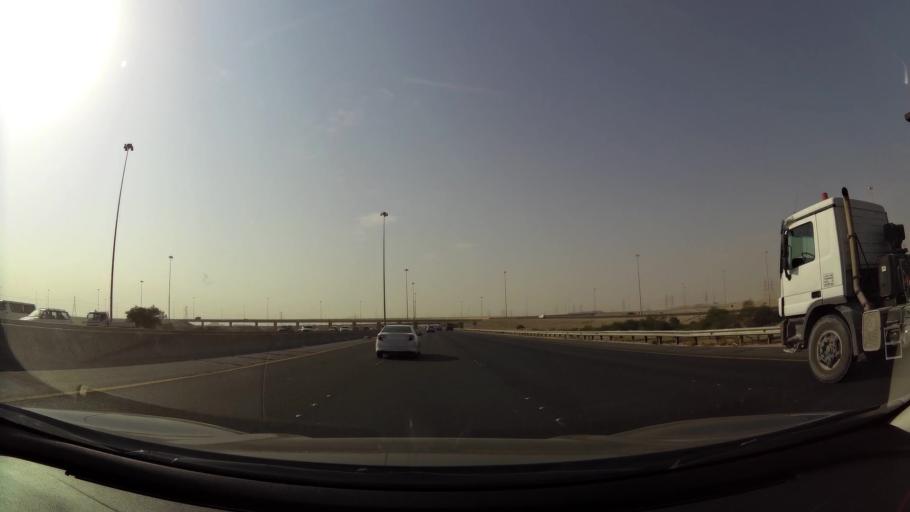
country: KW
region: Al Ahmadi
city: Al Ahmadi
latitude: 29.0388
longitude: 48.0931
